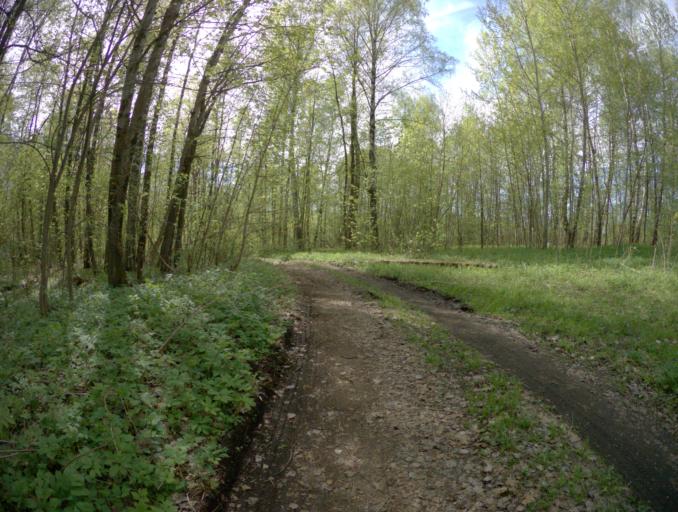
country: RU
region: Vladimir
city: Orgtrud
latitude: 56.1969
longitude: 40.5868
